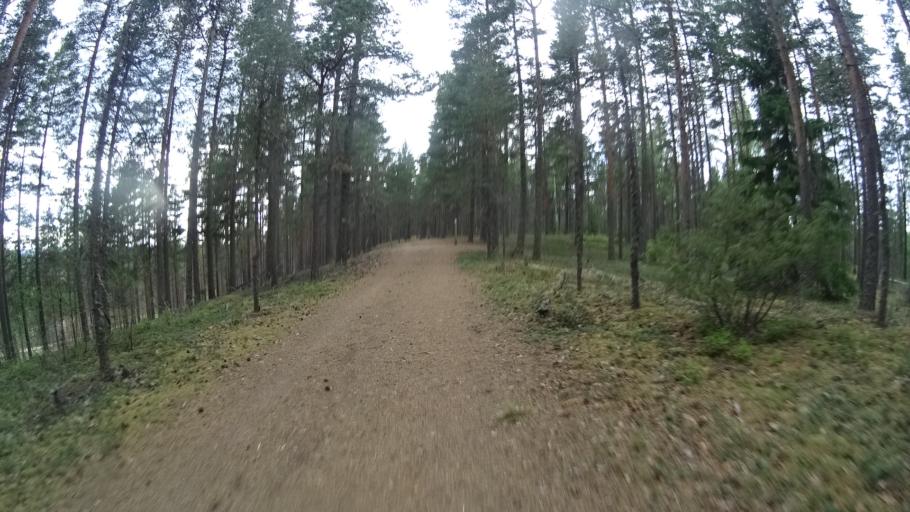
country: FI
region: Satakunta
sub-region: Pohjois-Satakunta
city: Jaemijaervi
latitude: 61.7733
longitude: 22.7320
